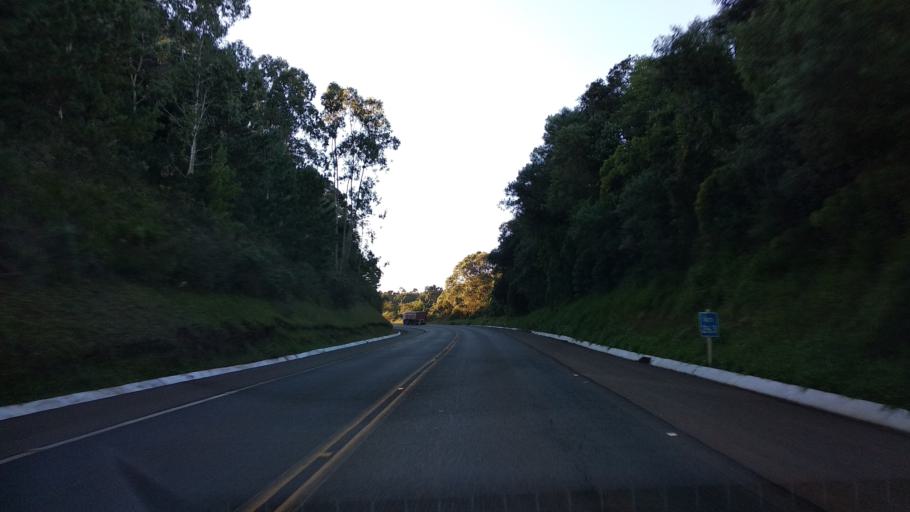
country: BR
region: Santa Catarina
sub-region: Correia Pinto
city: Correia Pinto
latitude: -27.6312
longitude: -50.6185
